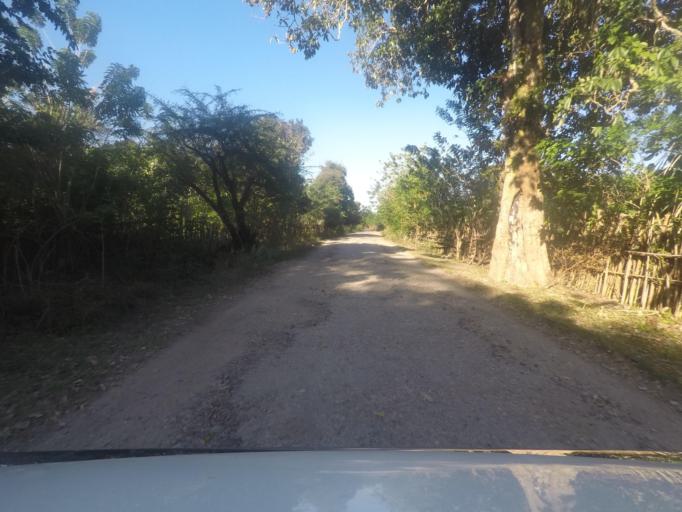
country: TL
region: Lautem
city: Lospalos
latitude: -8.4096
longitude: 127.1652
